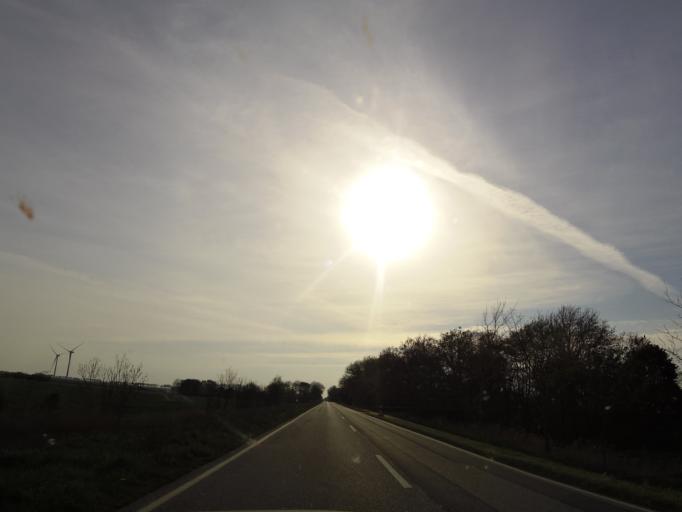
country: DE
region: Schleswig-Holstein
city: Galmsbull
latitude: 54.7754
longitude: 8.7803
